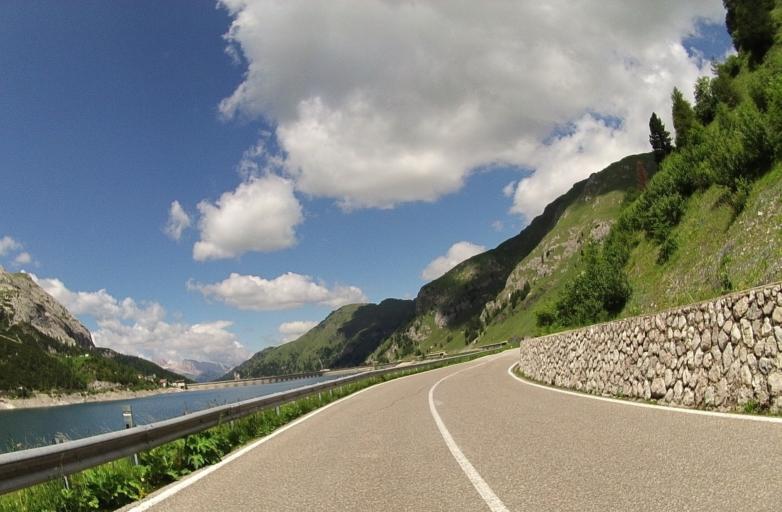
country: IT
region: Veneto
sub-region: Provincia di Belluno
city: Livinallongo del Col di Lana
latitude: 46.4581
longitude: 11.8760
